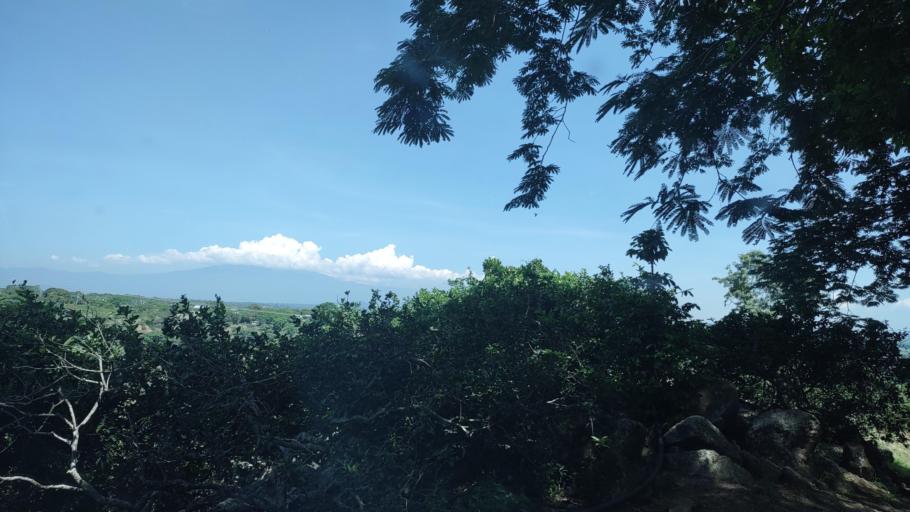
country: MX
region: Veracruz
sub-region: Emiliano Zapata
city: Dos Rios
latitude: 19.4300
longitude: -96.7940
